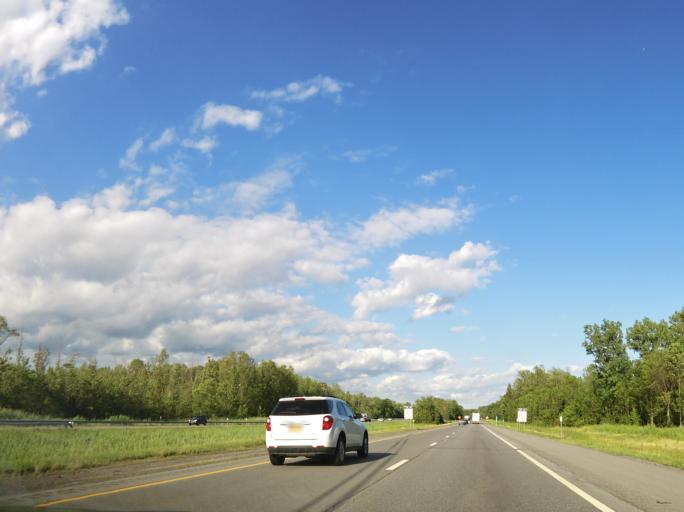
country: US
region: New York
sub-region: Erie County
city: Clarence
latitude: 42.9652
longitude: -78.5463
